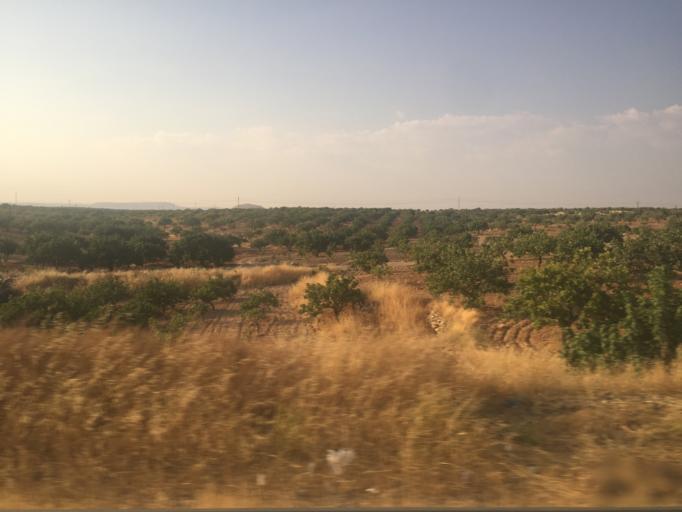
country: TR
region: Gaziantep
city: Nizip
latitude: 37.0161
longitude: 37.8856
